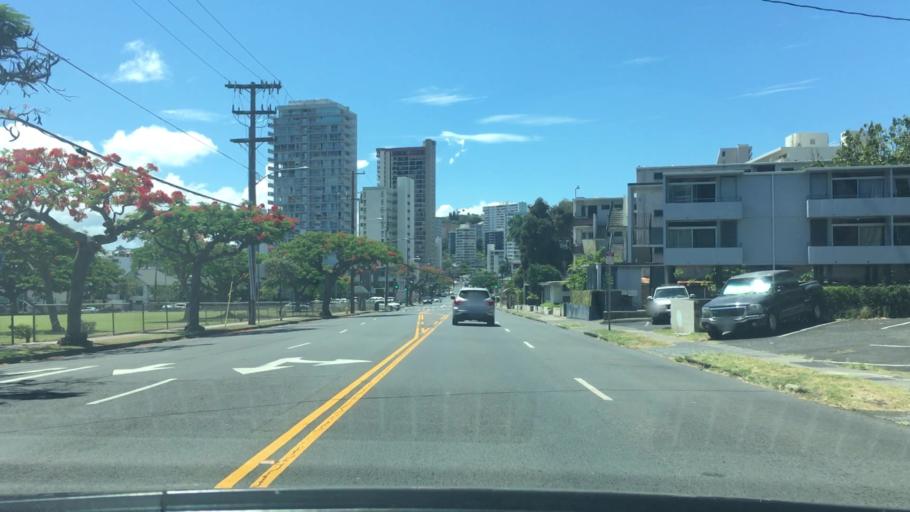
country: US
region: Hawaii
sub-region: Honolulu County
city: Honolulu
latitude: 21.3041
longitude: -157.8351
